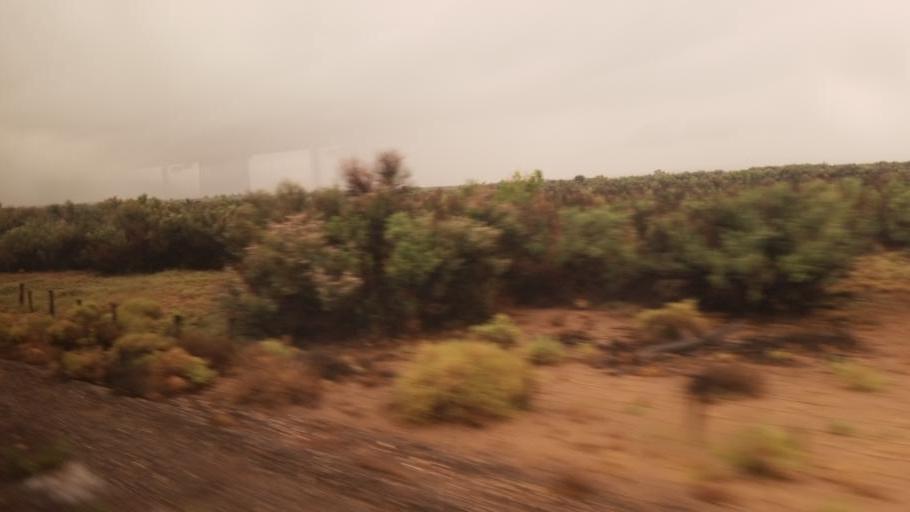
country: US
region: Arizona
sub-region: Navajo County
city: Joseph City
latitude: 34.9674
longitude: -110.4612
